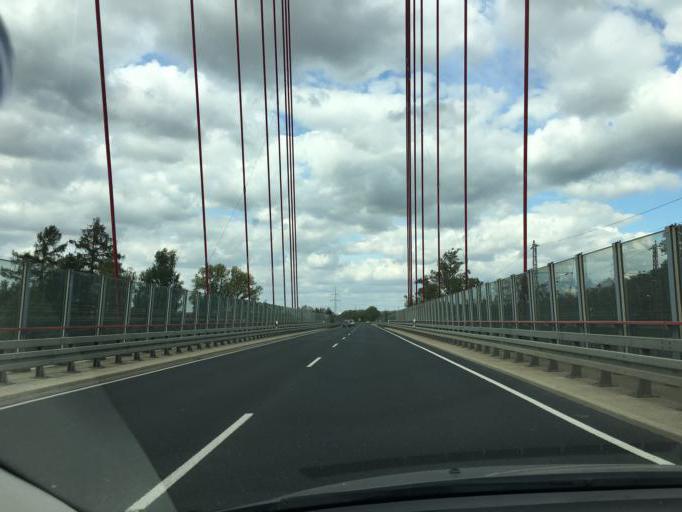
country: DE
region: Saxony
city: Coswig
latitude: 51.0970
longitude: 13.6044
